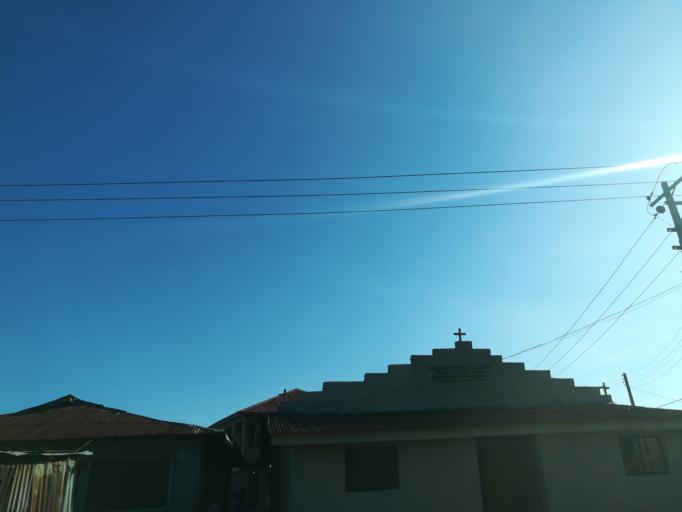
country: NG
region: Lagos
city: Ebute Ikorodu
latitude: 6.5393
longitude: 3.5503
